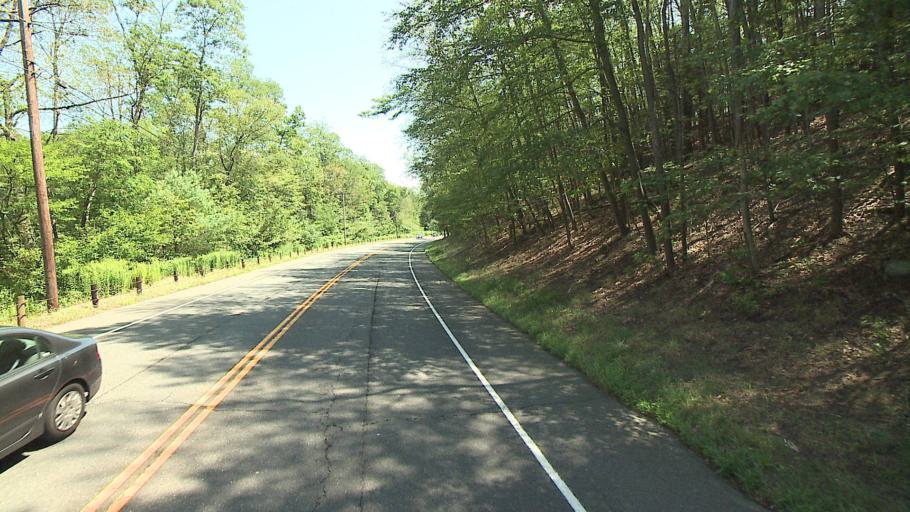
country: US
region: Connecticut
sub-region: Hartford County
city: Collinsville
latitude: 41.7751
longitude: -72.9082
